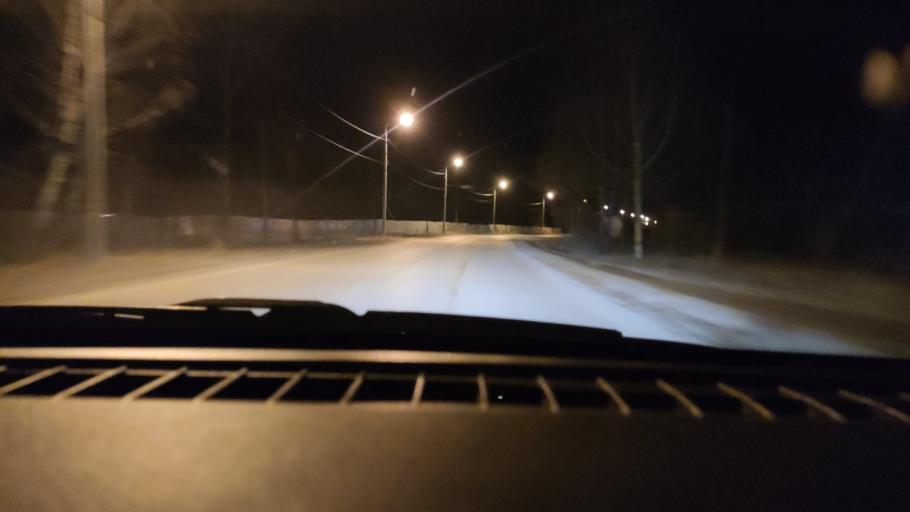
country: RU
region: Perm
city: Perm
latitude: 58.0392
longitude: 56.2637
